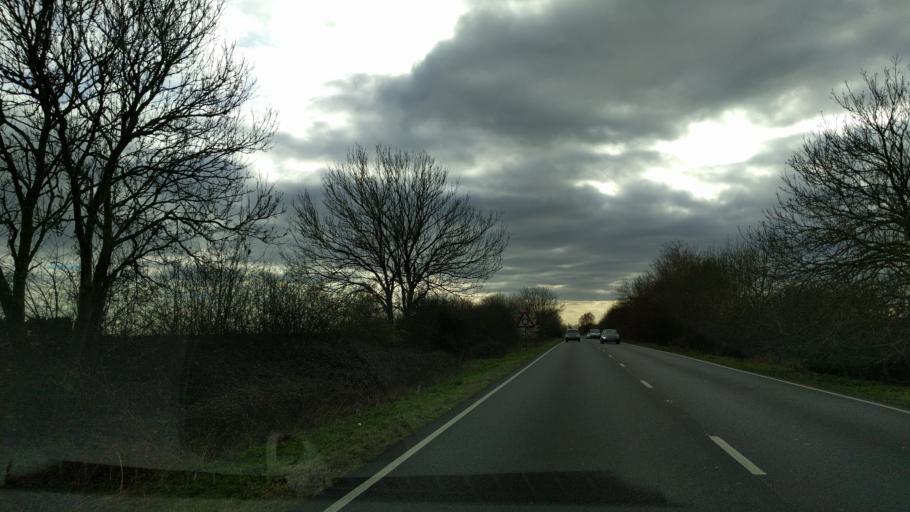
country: GB
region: England
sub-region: Cambridgeshire
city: Hemingford Grey
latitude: 52.3569
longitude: -0.1282
